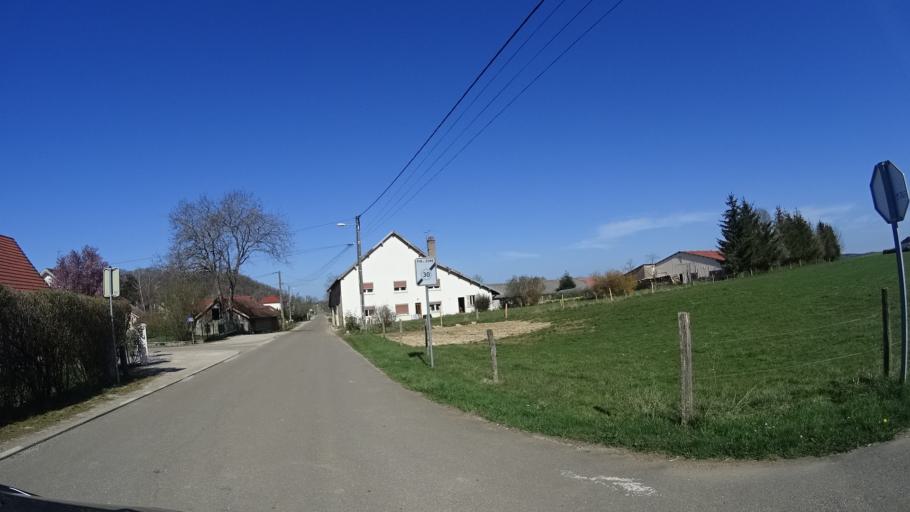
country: FR
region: Franche-Comte
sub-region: Departement du Doubs
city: Ornans
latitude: 47.1454
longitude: 6.0854
